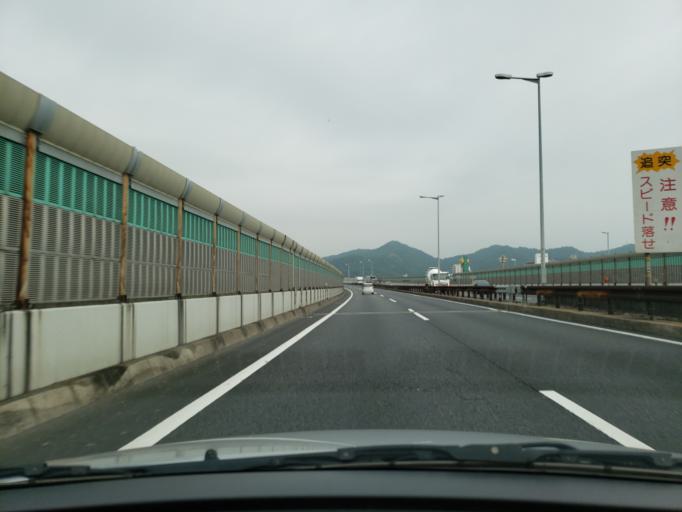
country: JP
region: Hyogo
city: Himeji
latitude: 34.8161
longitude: 134.6694
